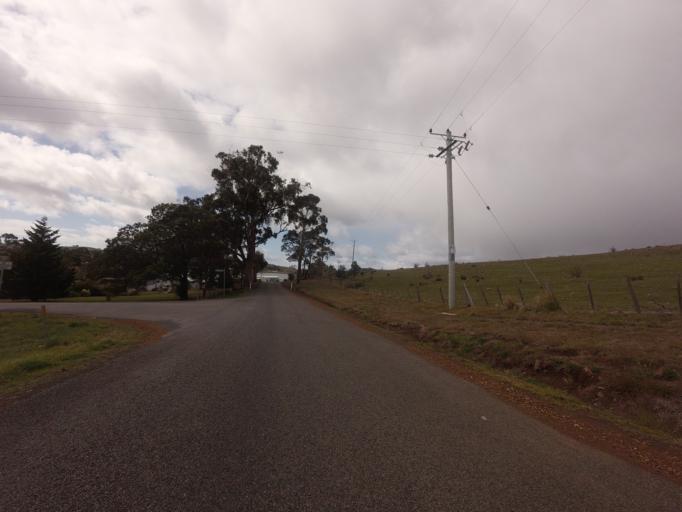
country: AU
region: Tasmania
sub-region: Sorell
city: Sorell
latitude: -42.5430
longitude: 147.9108
